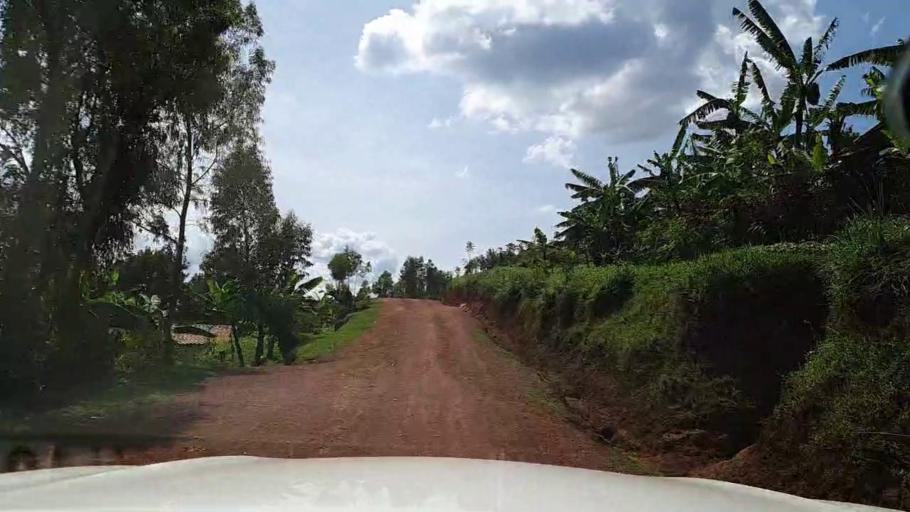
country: RW
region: Southern Province
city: Butare
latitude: -2.7442
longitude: 29.6992
